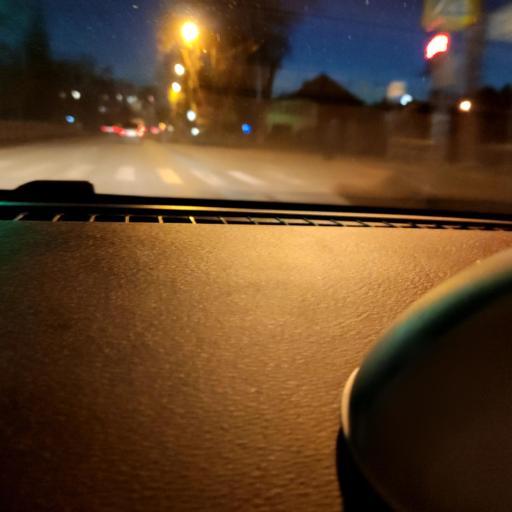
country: RU
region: Samara
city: Smyshlyayevka
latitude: 53.2314
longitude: 50.3056
